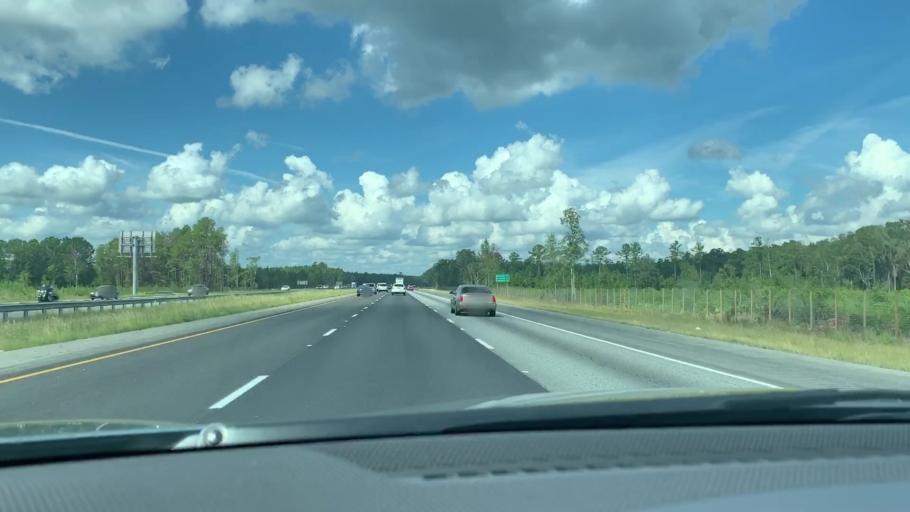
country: US
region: Georgia
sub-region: Camden County
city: Kingsland
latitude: 30.8628
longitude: -81.6797
